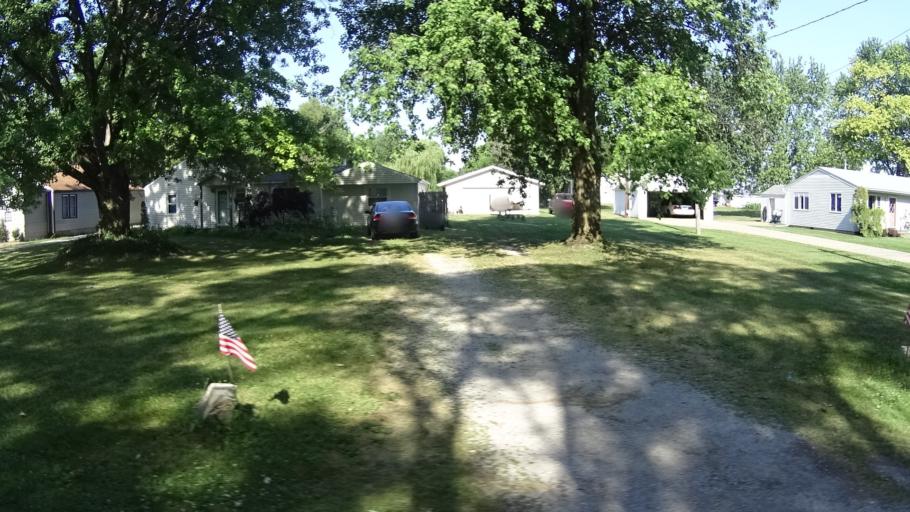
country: US
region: Ohio
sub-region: Huron County
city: Bellevue
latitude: 41.3733
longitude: -82.7952
